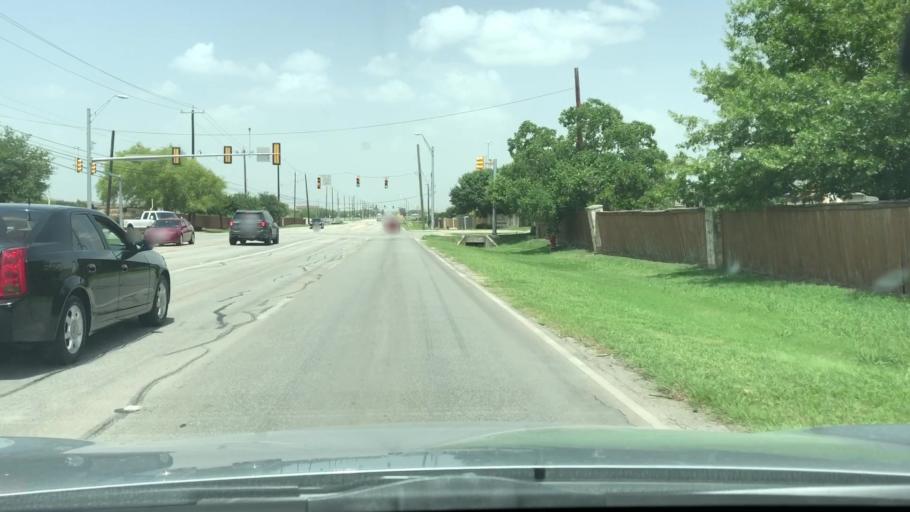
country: US
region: Texas
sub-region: Bexar County
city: Selma
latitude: 29.5860
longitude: -98.3281
